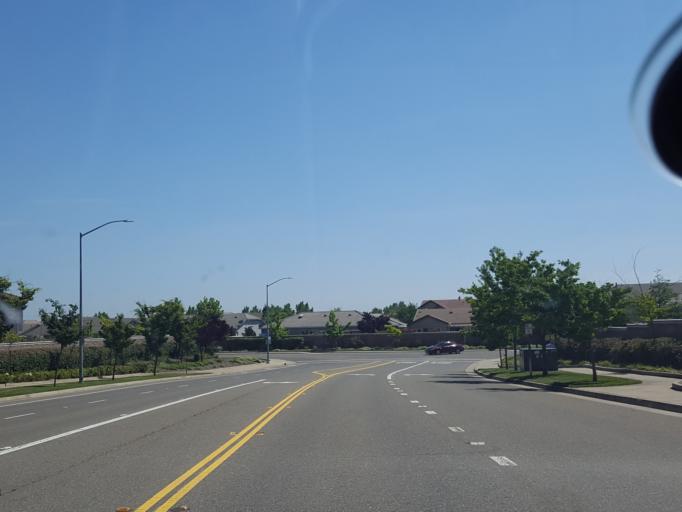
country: US
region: California
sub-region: Sacramento County
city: Rancho Cordova
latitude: 38.5821
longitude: -121.2704
